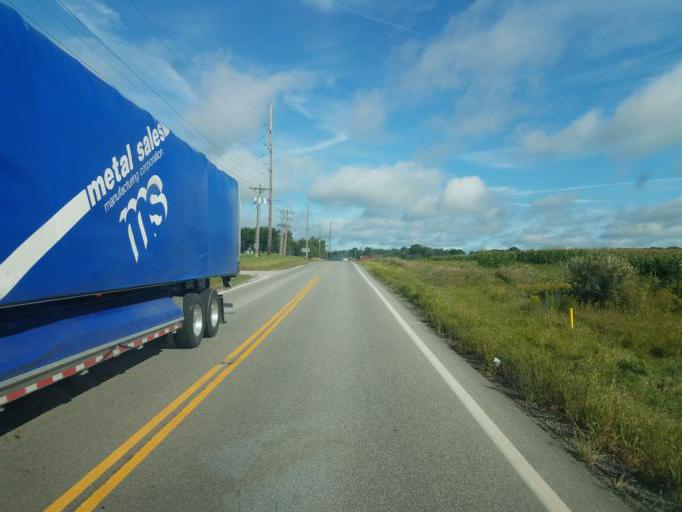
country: US
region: Ohio
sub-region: Wayne County
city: West Salem
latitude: 41.0178
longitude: -82.1209
